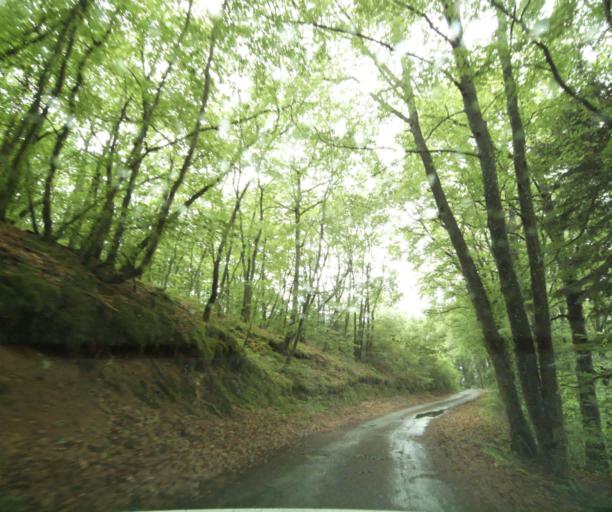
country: FR
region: Bourgogne
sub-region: Departement de Saone-et-Loire
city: Matour
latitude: 46.4512
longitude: 4.4661
